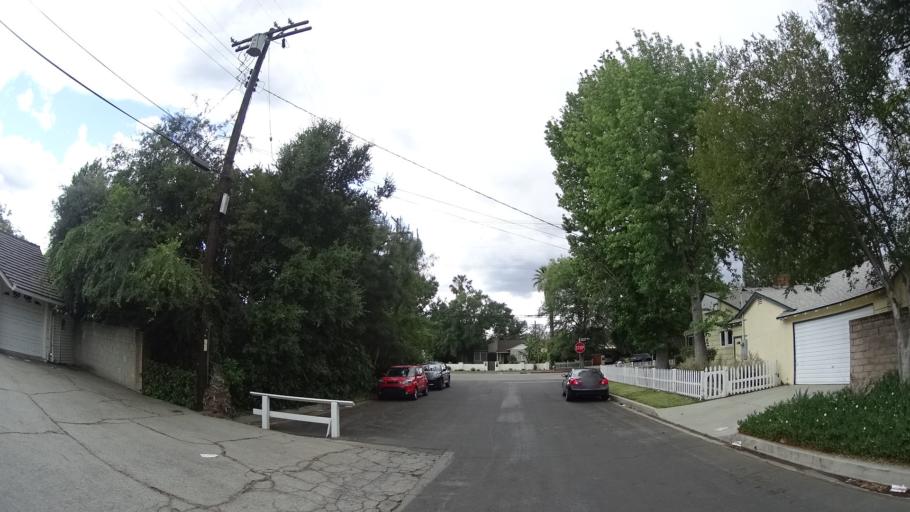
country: US
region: California
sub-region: Los Angeles County
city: Sherman Oaks
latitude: 34.1622
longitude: -118.4220
